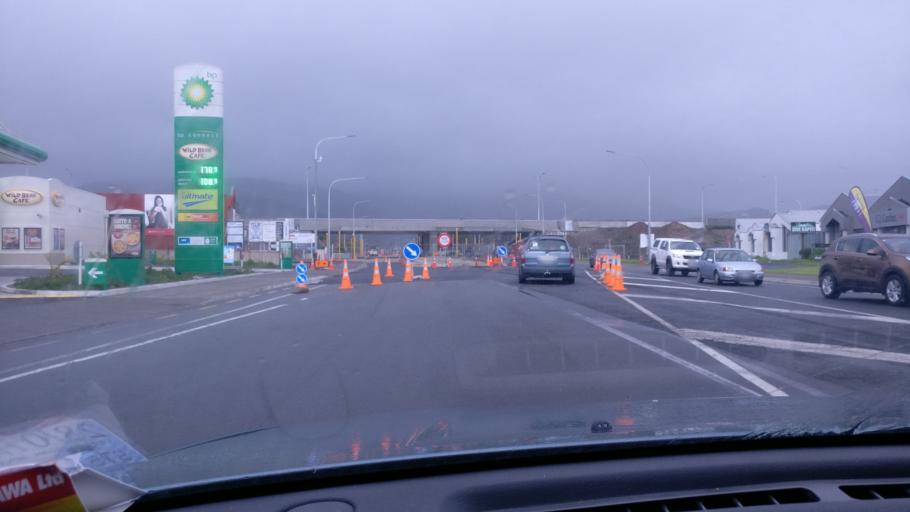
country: NZ
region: Wellington
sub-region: Kapiti Coast District
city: Paraparaumu
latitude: -40.9073
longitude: 174.9988
